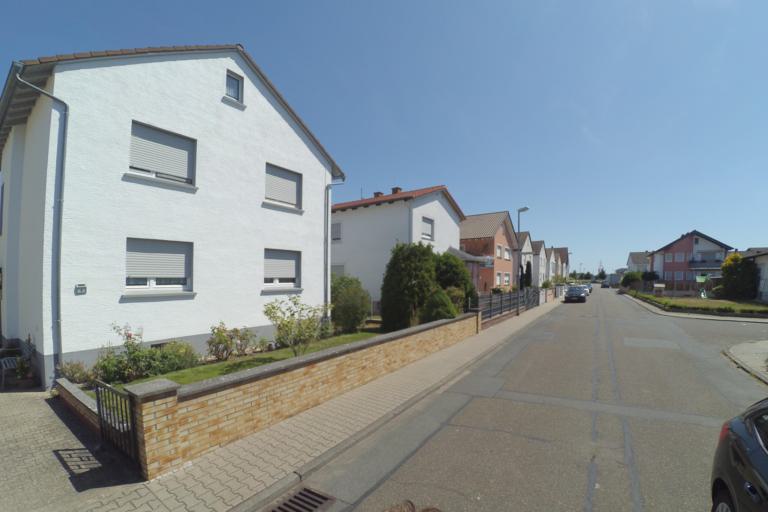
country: DE
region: Hesse
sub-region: Regierungsbezirk Darmstadt
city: Riedstadt
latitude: 49.8363
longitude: 8.4768
